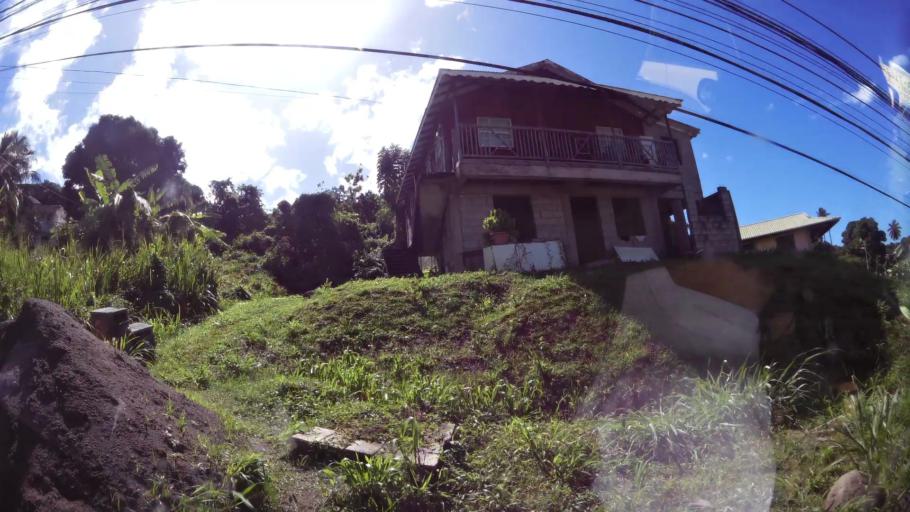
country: DM
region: Saint John
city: Portsmouth
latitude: 15.5530
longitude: -61.4570
